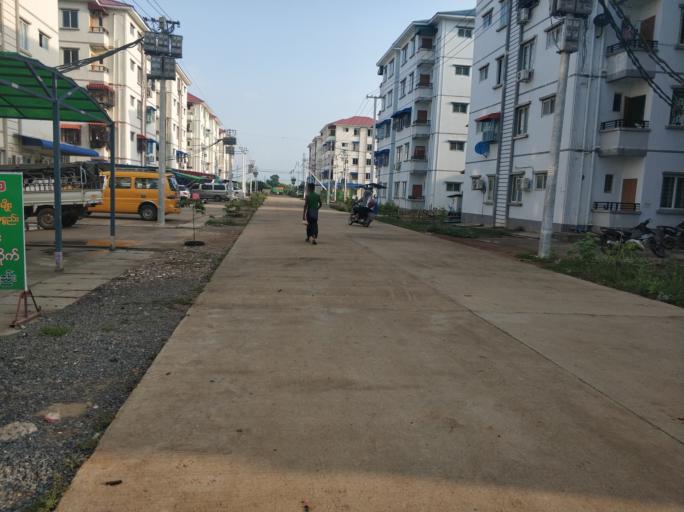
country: MM
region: Mandalay
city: Mandalay
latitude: 21.9160
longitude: 96.1344
